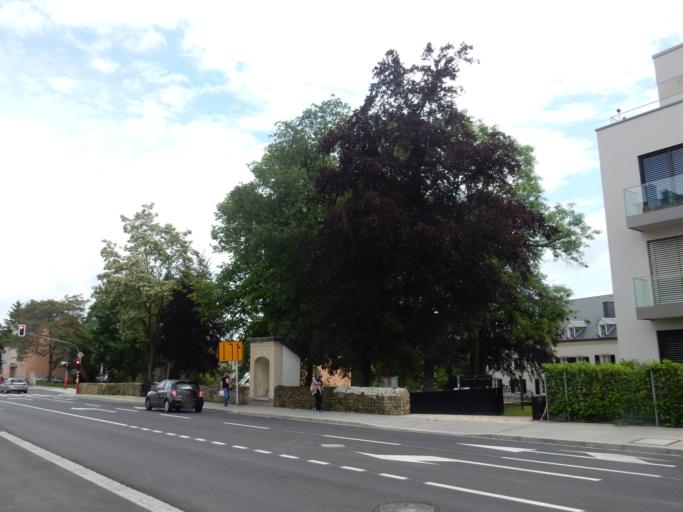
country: LU
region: Luxembourg
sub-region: Canton de Luxembourg
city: Strassen
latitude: 49.6055
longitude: 6.0966
